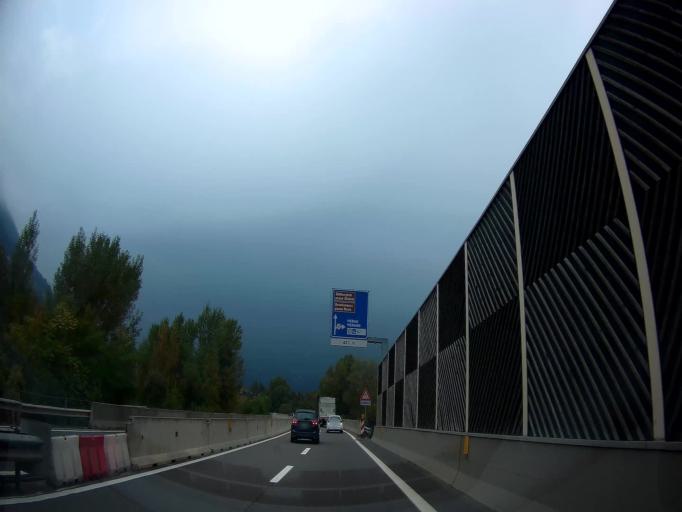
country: IT
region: Trentino-Alto Adige
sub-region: Bolzano
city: Marlengo
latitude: 46.6638
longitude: 11.1444
